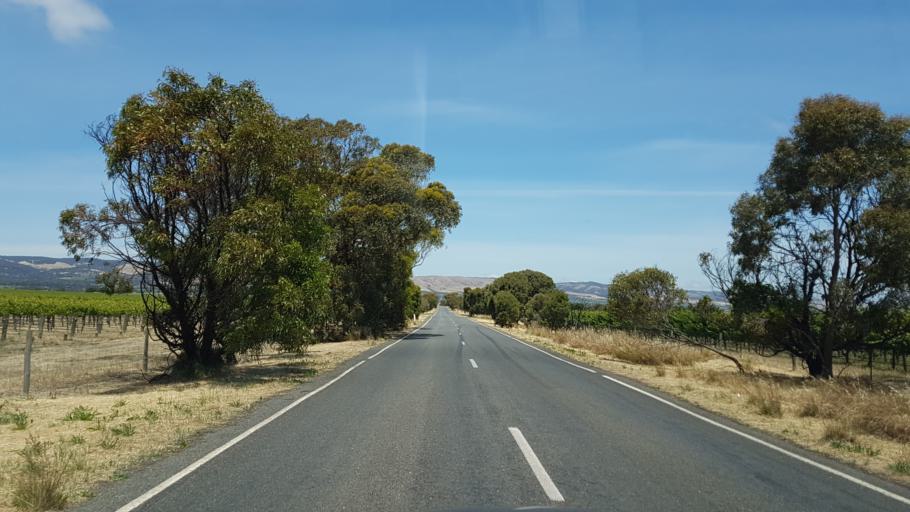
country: AU
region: South Australia
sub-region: Onkaparinga
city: McLaren Vale
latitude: -35.2348
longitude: 138.5193
